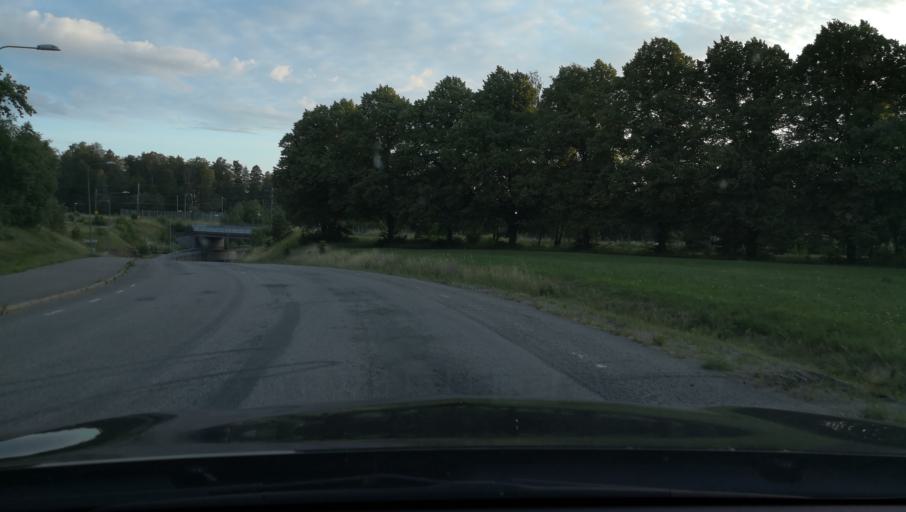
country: SE
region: Uppsala
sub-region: Uppsala Kommun
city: Vattholma
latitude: 60.0233
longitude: 17.7322
